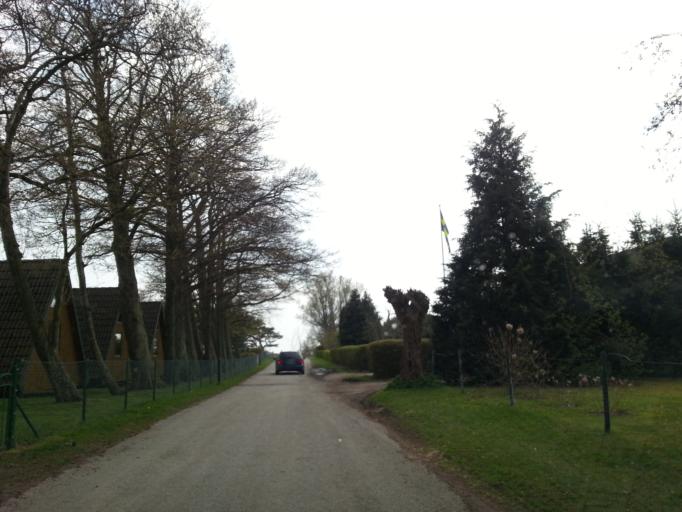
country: SE
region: Skane
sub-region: Trelleborgs Kommun
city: Trelleborg
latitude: 55.3545
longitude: 13.2423
